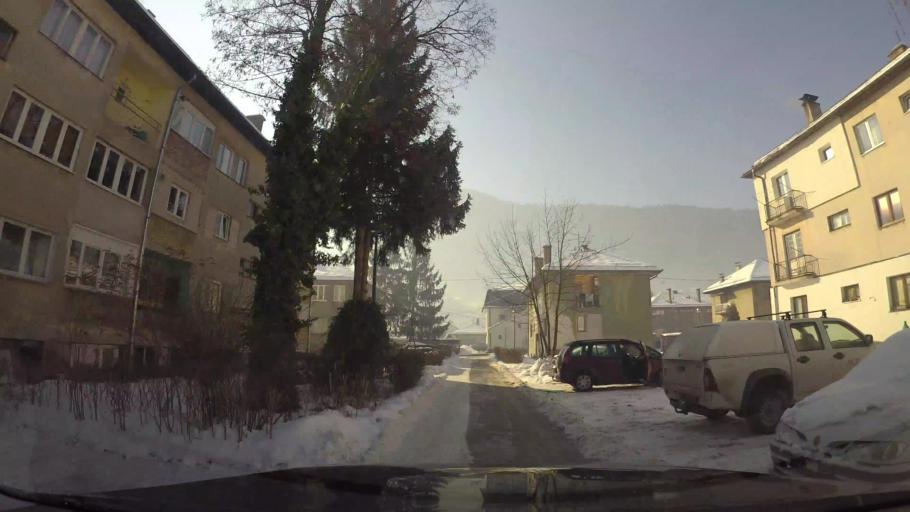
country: BA
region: Federation of Bosnia and Herzegovina
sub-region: Kanton Sarajevo
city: Sarajevo
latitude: 43.7991
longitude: 18.3085
